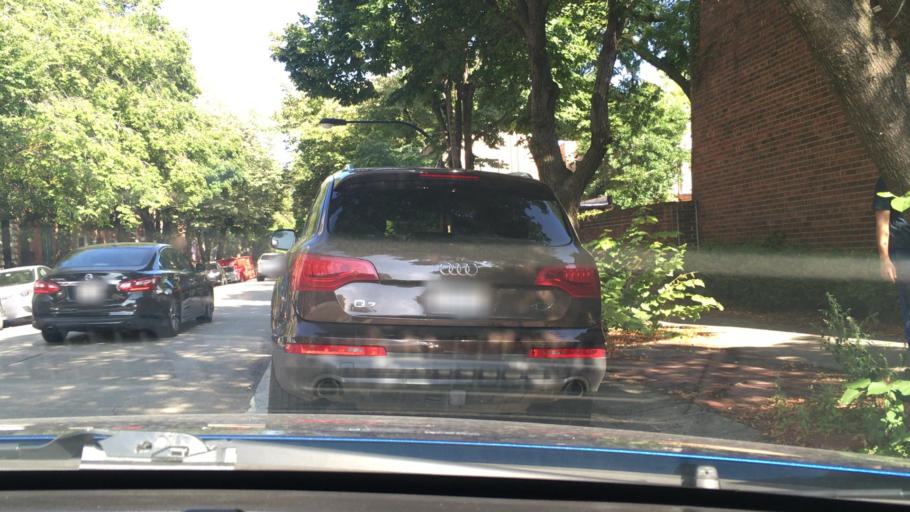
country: US
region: Illinois
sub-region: Cook County
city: Chicago
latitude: 41.8716
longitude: -87.6639
